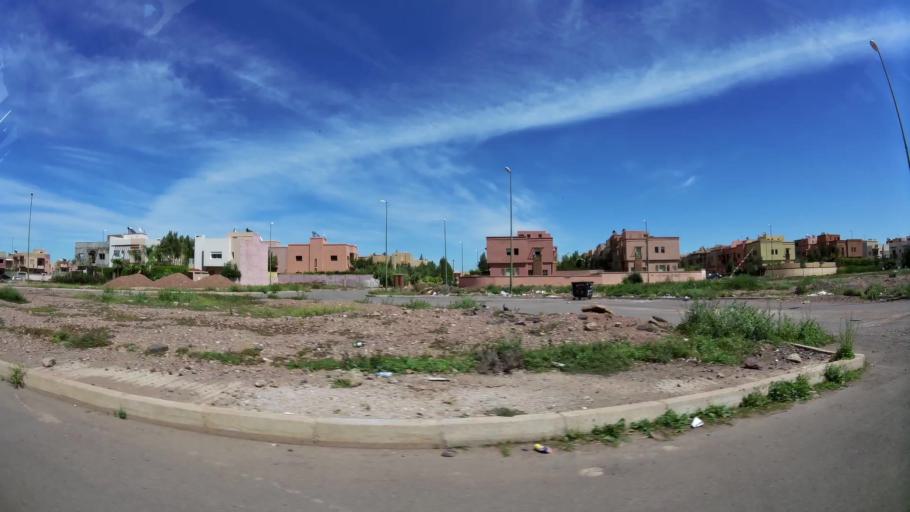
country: MA
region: Marrakech-Tensift-Al Haouz
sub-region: Marrakech
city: Marrakesh
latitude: 31.6540
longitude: -8.0812
